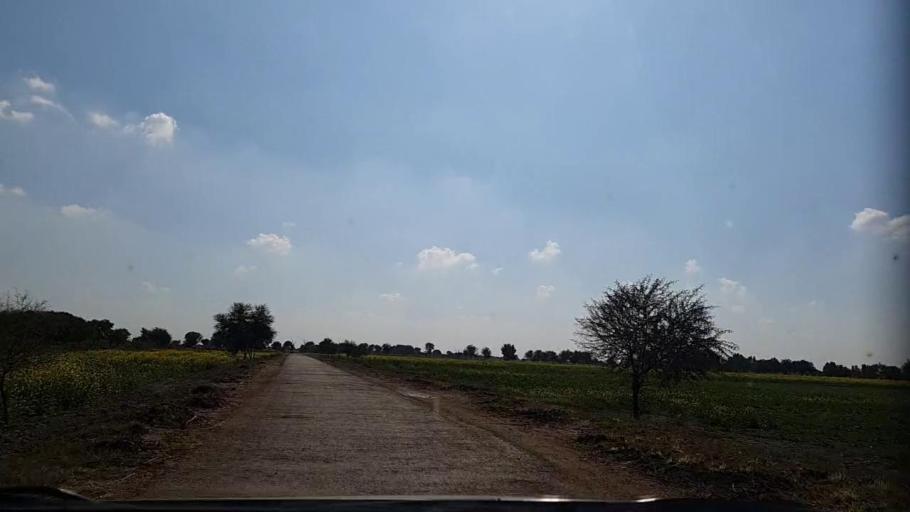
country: PK
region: Sindh
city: Pithoro
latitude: 25.6687
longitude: 69.4618
